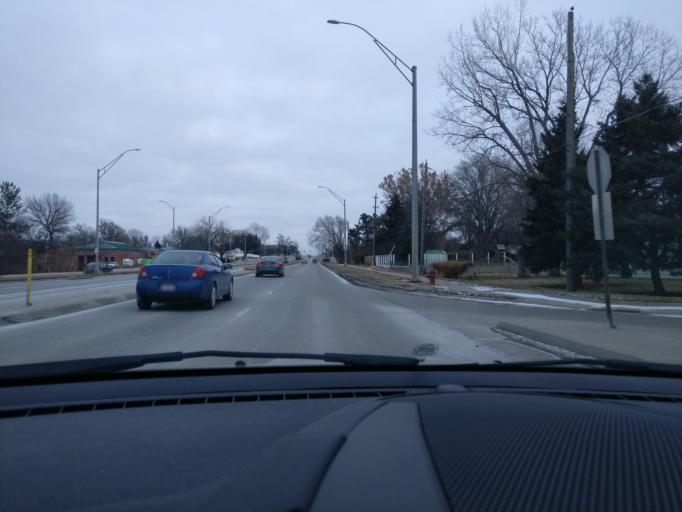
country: US
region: Nebraska
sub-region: Lancaster County
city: Lincoln
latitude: 40.8134
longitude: -96.6134
